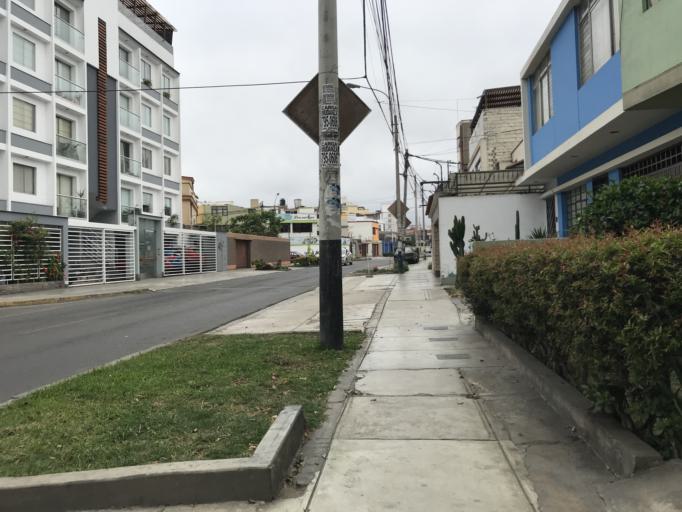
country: PE
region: Lima
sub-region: Lima
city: San Isidro
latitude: -12.0757
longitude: -77.0738
